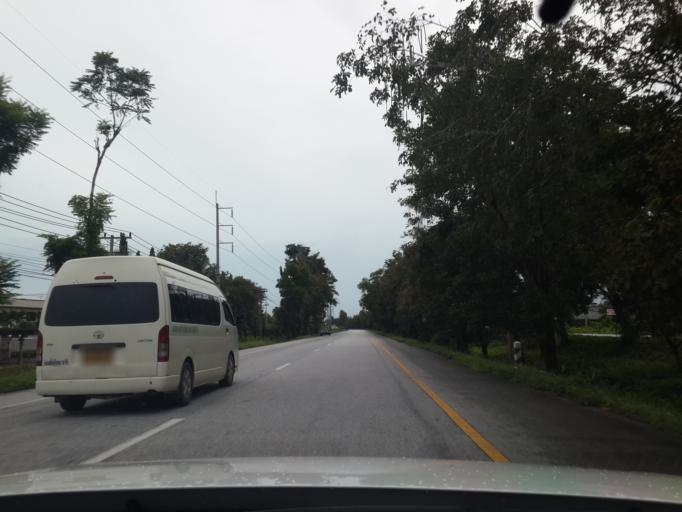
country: TH
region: Songkhla
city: Chana
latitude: 6.9201
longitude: 100.7516
